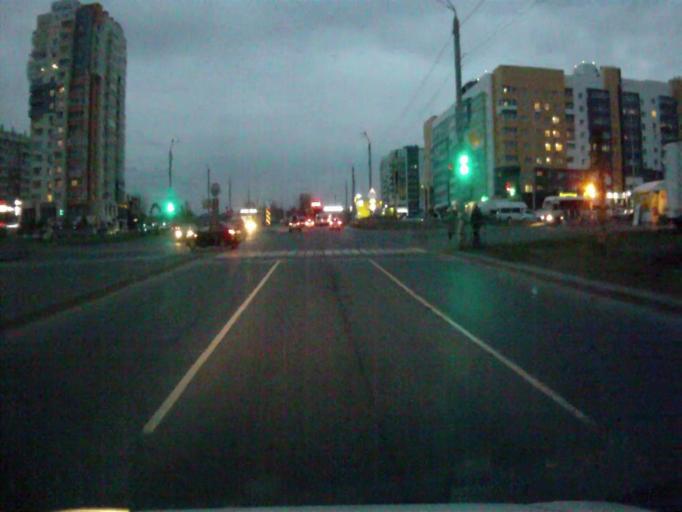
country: RU
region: Chelyabinsk
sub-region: Gorod Chelyabinsk
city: Chelyabinsk
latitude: 55.1637
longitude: 61.2949
